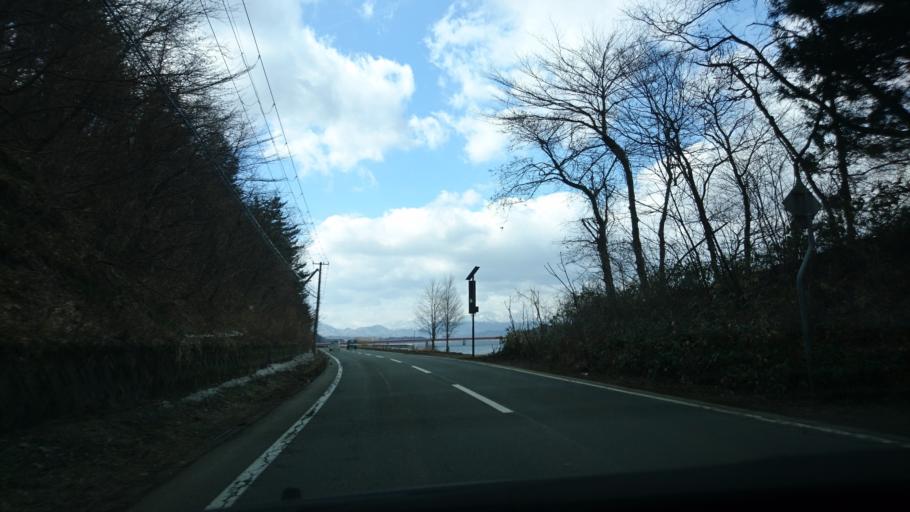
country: JP
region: Iwate
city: Shizukuishi
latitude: 39.6831
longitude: 141.0284
